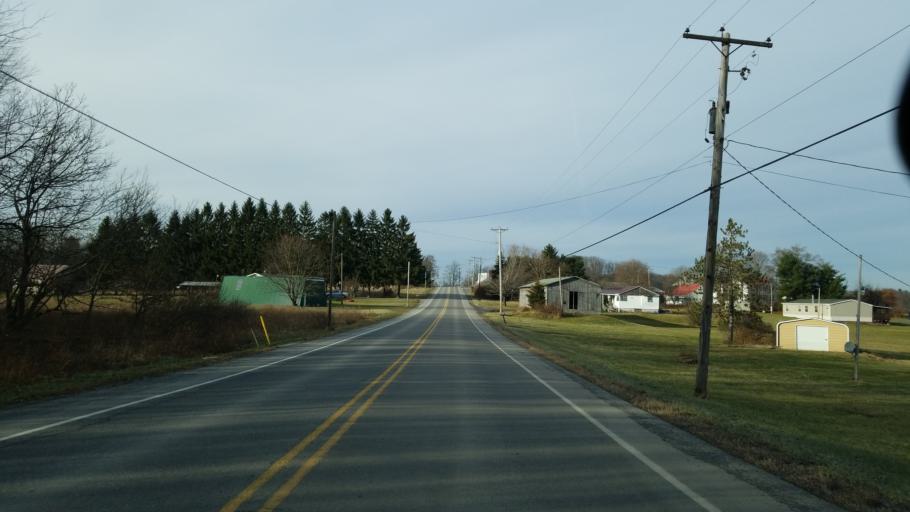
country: US
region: Pennsylvania
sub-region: Clearfield County
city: Curwensville
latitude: 41.0180
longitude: -78.6434
